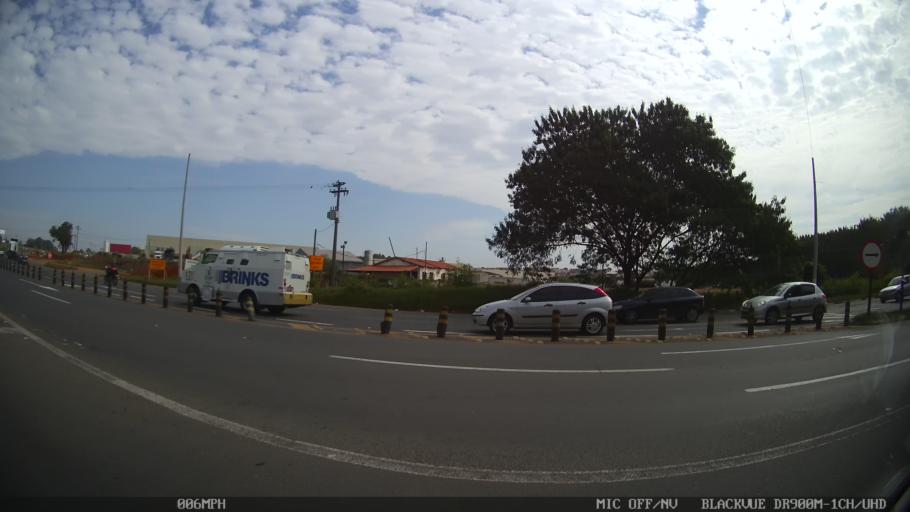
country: BR
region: Sao Paulo
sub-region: Paulinia
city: Paulinia
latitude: -22.8045
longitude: -47.1777
